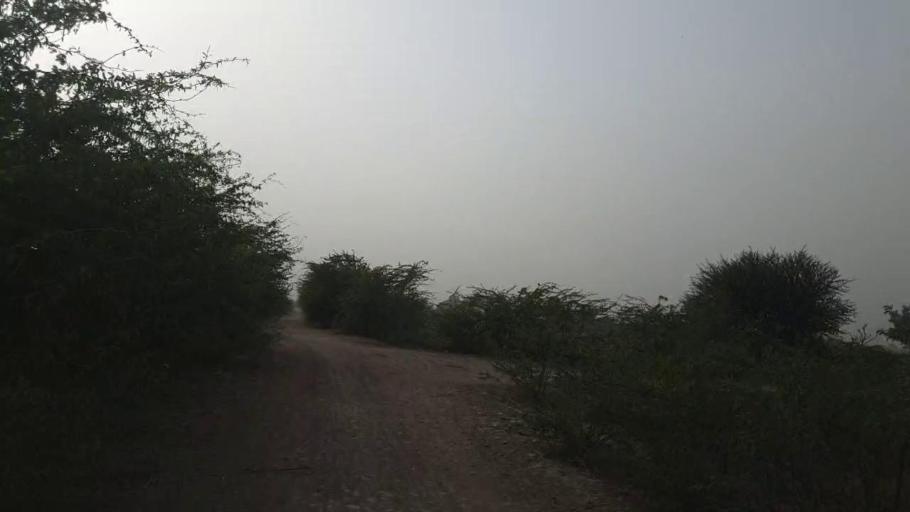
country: PK
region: Sindh
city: Kunri
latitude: 25.0669
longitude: 69.4652
